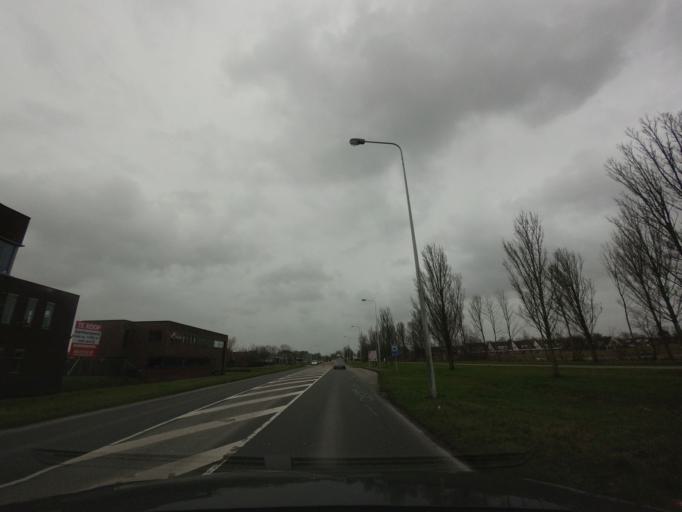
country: NL
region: Friesland
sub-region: Gemeente Franekeradeel
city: Franeker
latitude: 53.1985
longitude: 5.5413
